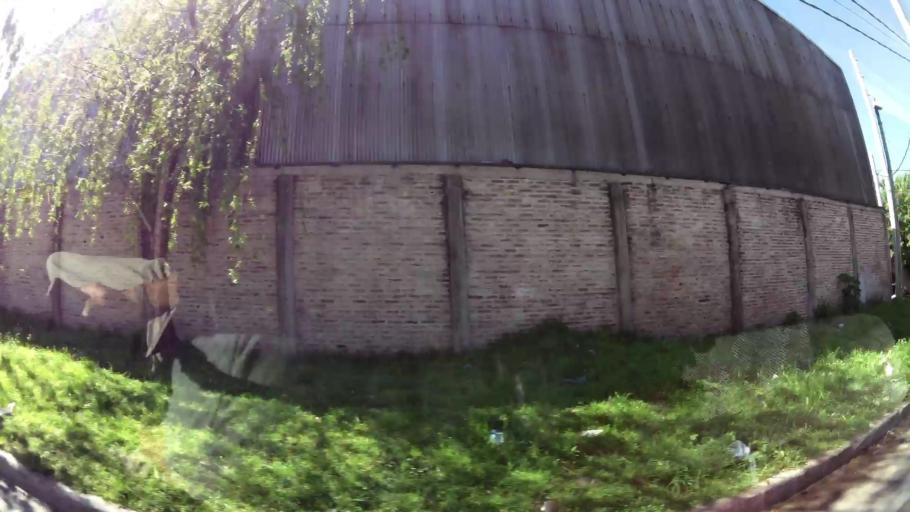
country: AR
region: Buenos Aires
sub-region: Partido de Quilmes
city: Quilmes
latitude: -34.6889
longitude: -58.3018
